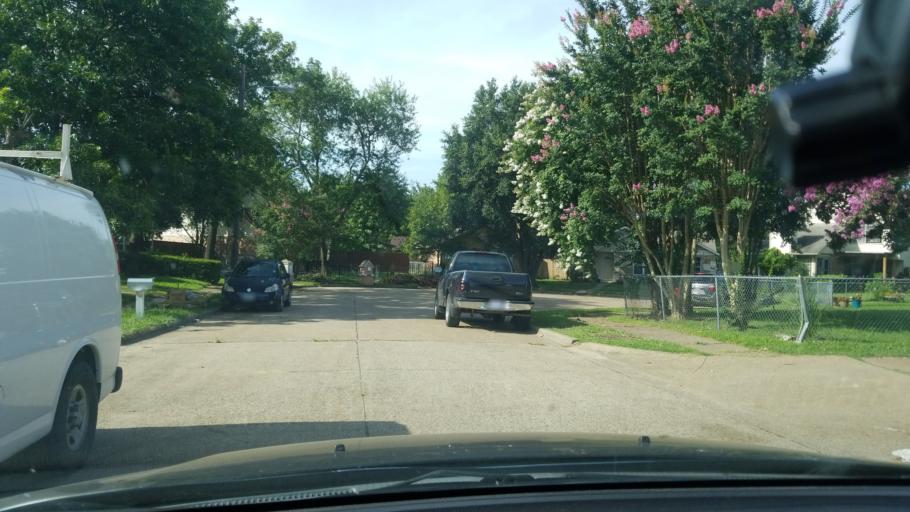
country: US
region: Texas
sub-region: Dallas County
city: Balch Springs
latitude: 32.7172
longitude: -96.6403
